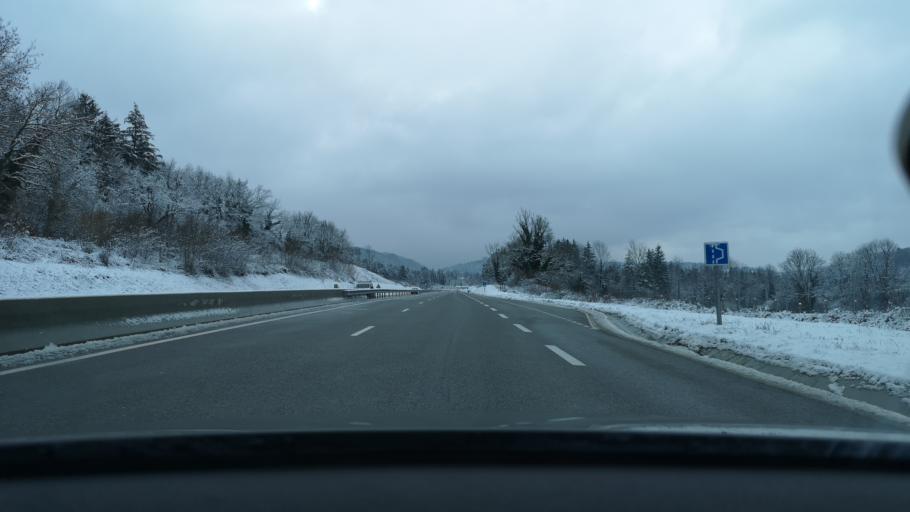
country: FR
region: Rhone-Alpes
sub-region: Departement de l'Ain
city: Dortan
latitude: 46.3168
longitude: 5.6707
